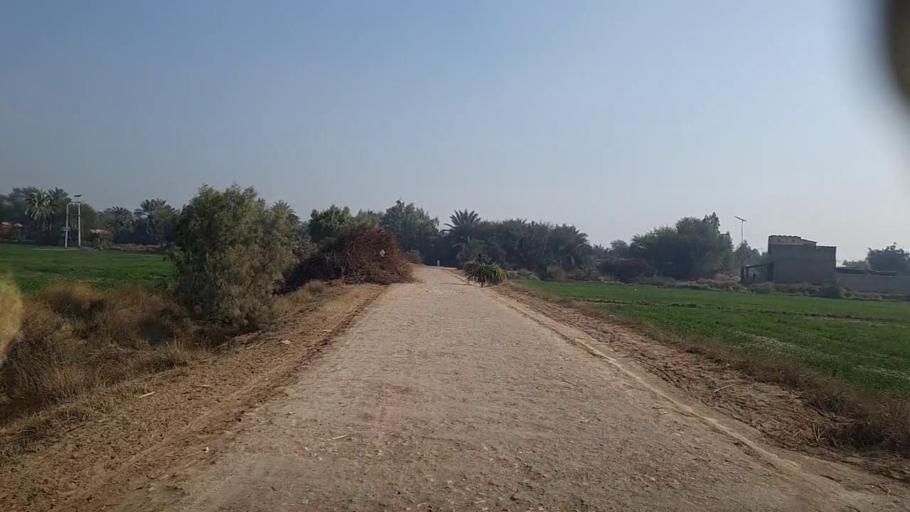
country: PK
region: Sindh
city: Khairpur
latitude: 27.9387
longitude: 69.6706
